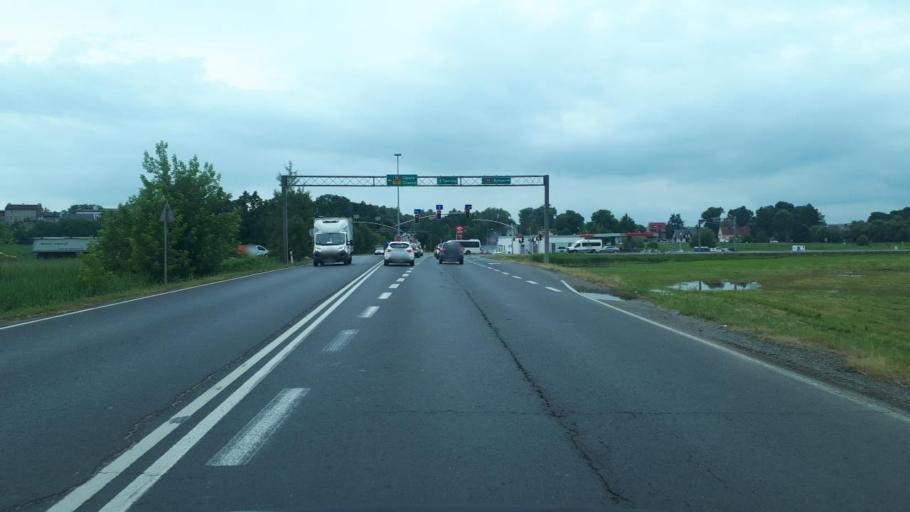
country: PL
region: Silesian Voivodeship
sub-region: Powiat gliwicki
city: Pyskowice
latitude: 50.3945
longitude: 18.6345
